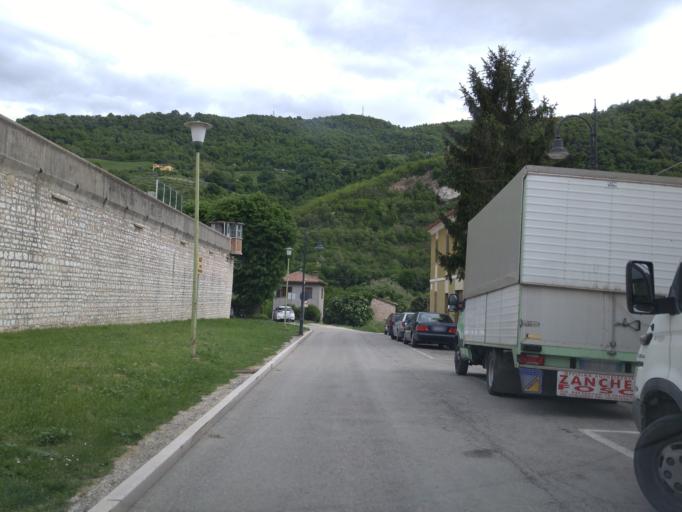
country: IT
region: The Marches
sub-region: Provincia di Pesaro e Urbino
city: Fossombrone
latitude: 43.6863
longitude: 12.8111
